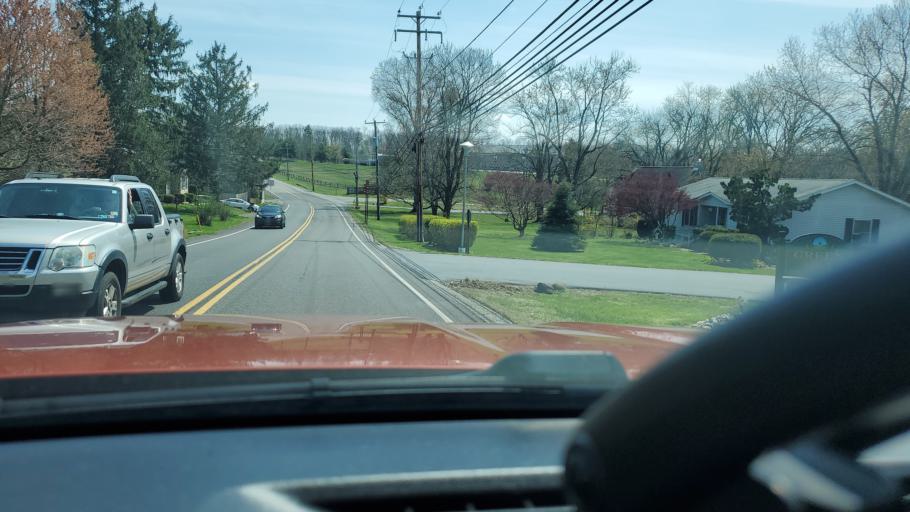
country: US
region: Pennsylvania
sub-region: Montgomery County
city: Red Hill
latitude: 40.3489
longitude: -75.4809
